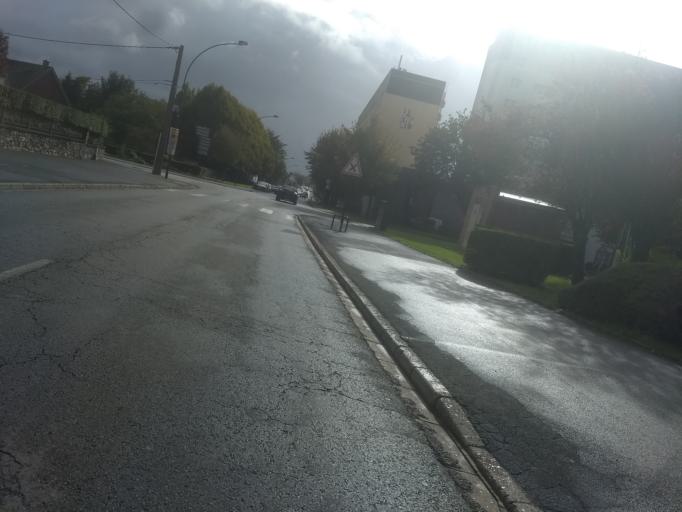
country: FR
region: Nord-Pas-de-Calais
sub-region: Departement du Pas-de-Calais
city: Achicourt
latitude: 50.2725
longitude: 2.7674
